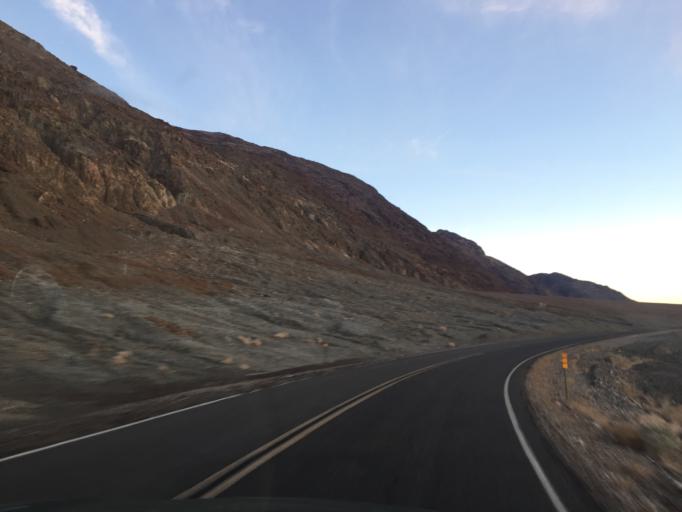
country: US
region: Nevada
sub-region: Nye County
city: Beatty
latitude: 36.2204
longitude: -116.7737
